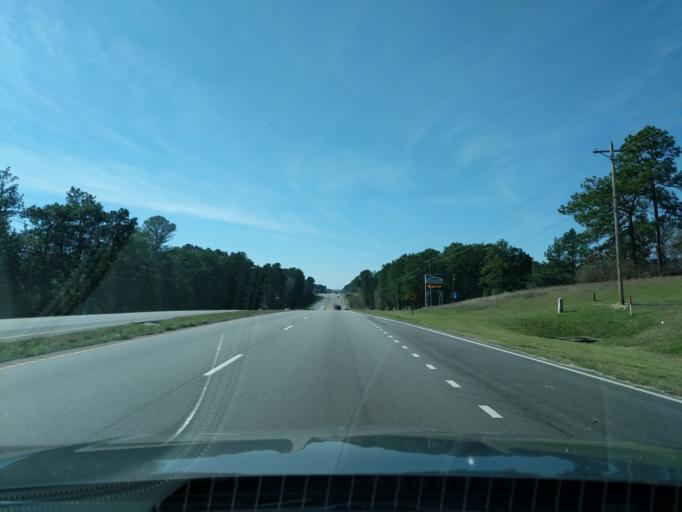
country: US
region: South Carolina
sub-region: Aiken County
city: Gloverville
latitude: 33.5336
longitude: -81.8389
